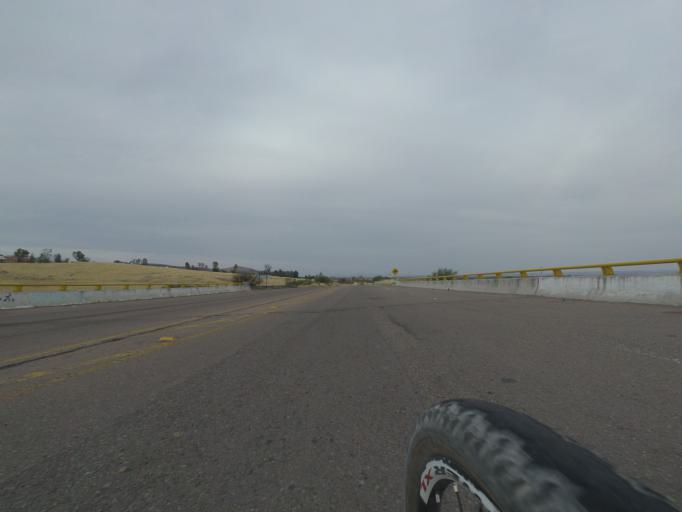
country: MX
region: Aguascalientes
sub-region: Aguascalientes
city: La Loma de los Negritos
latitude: 21.8909
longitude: -102.3985
